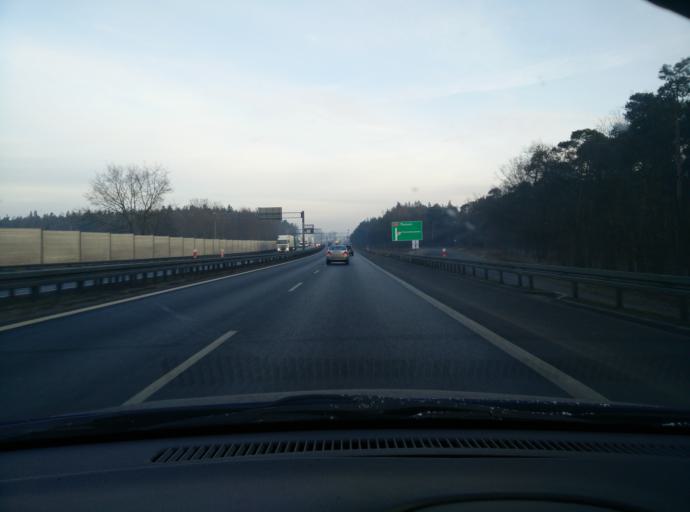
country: PL
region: Greater Poland Voivodeship
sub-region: Powiat poznanski
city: Kornik
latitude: 52.3024
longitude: 17.0485
